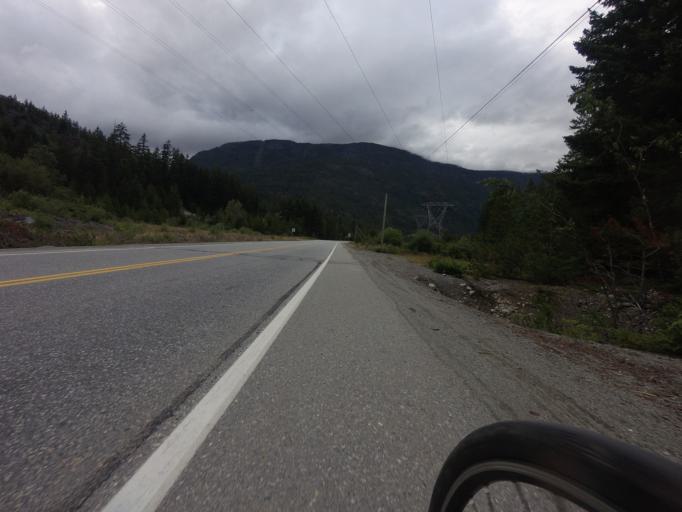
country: CA
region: British Columbia
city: Pemberton
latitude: 50.2641
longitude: -122.8660
